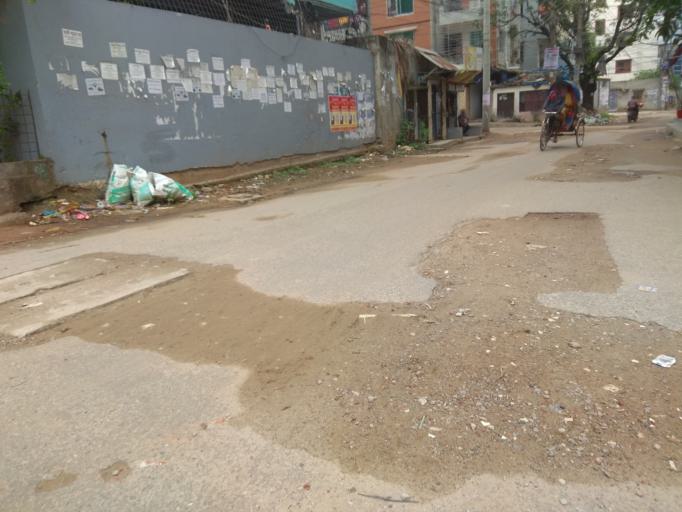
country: BD
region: Dhaka
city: Azimpur
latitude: 23.8054
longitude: 90.3544
